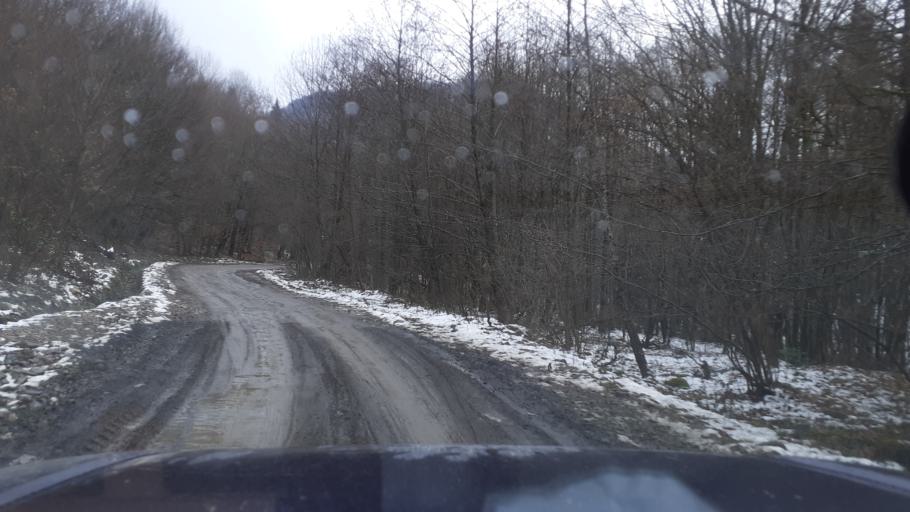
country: RU
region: Krasnodarskiy
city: Neftegorsk
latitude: 44.0664
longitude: 39.7255
